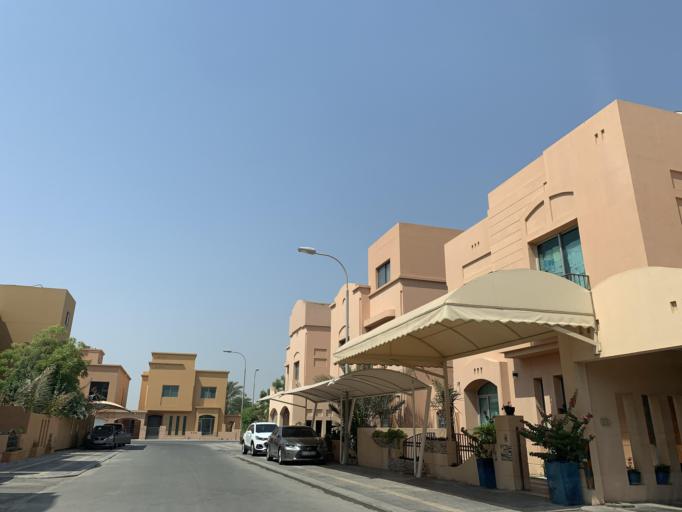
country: BH
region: Manama
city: Jidd Hafs
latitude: 26.2114
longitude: 50.5212
